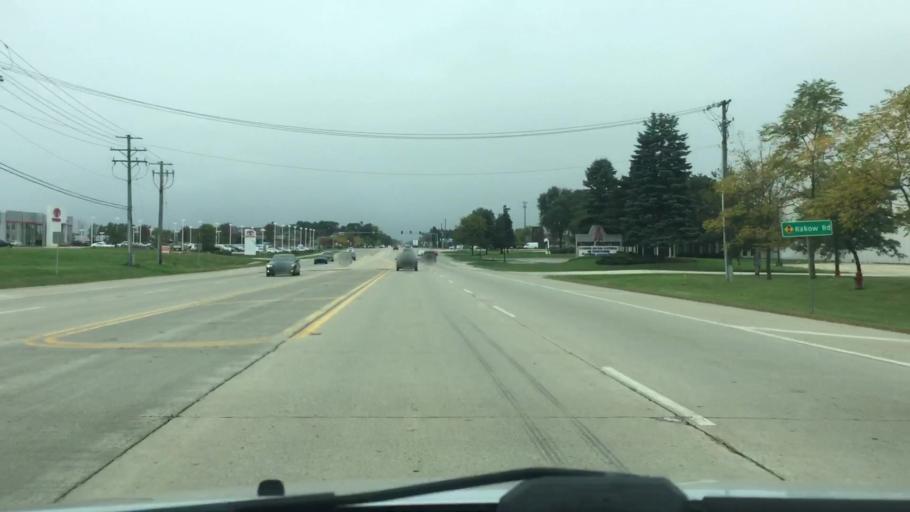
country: US
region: Illinois
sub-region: McHenry County
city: Crystal Lake
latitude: 42.2148
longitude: -88.2866
